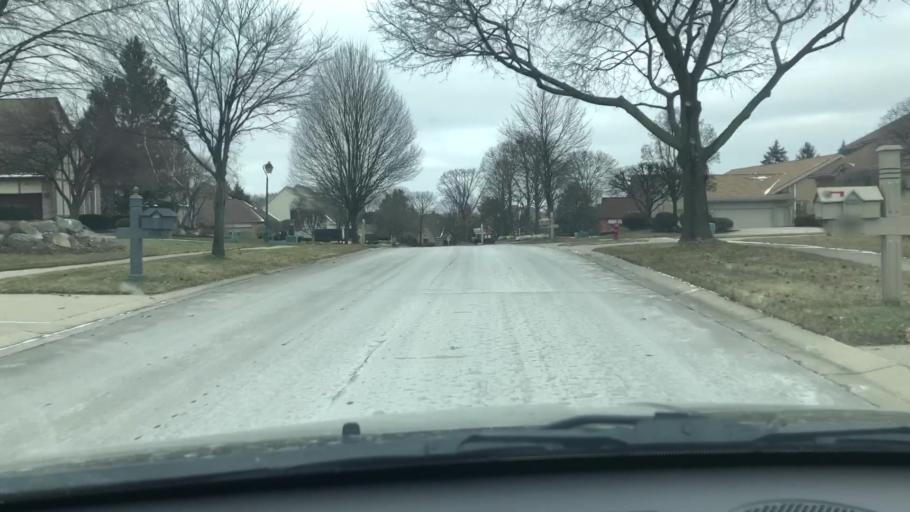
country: US
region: Michigan
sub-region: Oakland County
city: Rochester
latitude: 42.6907
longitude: -83.1150
